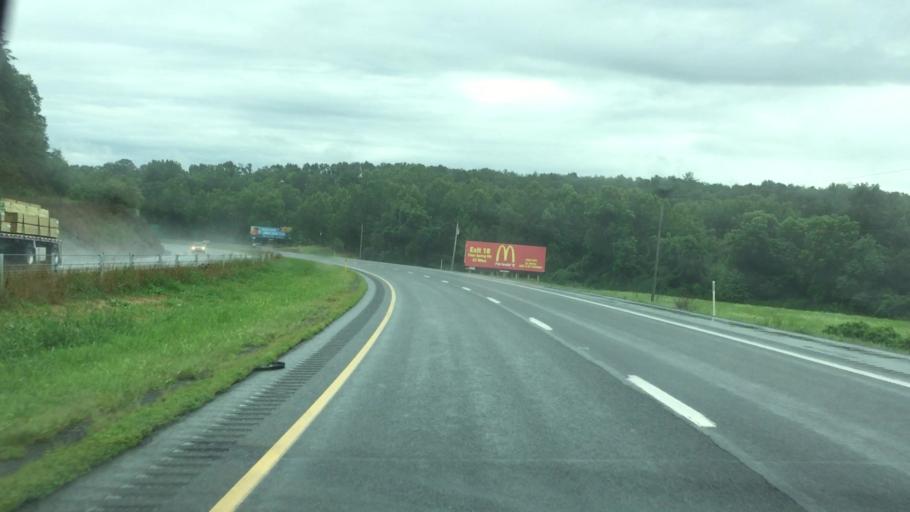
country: US
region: Maryland
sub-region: Washington County
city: Hancock
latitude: 39.7854
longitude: -78.2104
